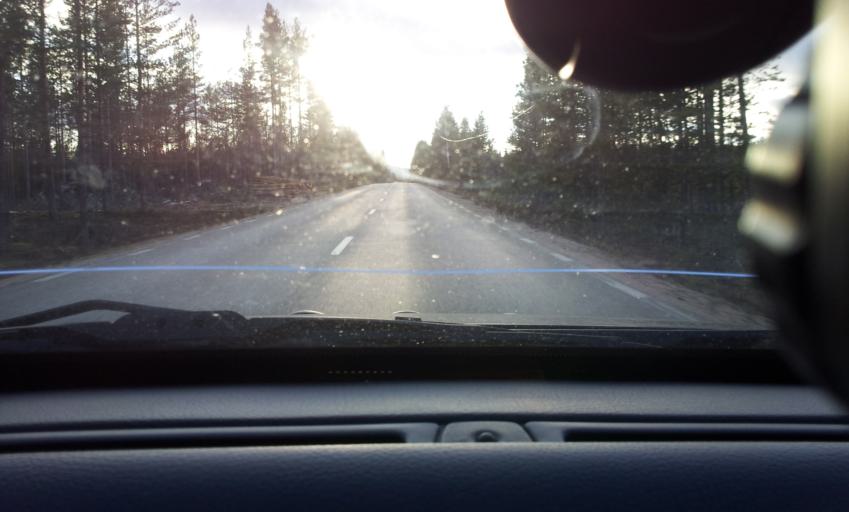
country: SE
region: Jaemtland
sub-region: Harjedalens Kommun
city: Sveg
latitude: 62.1236
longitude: 15.0063
